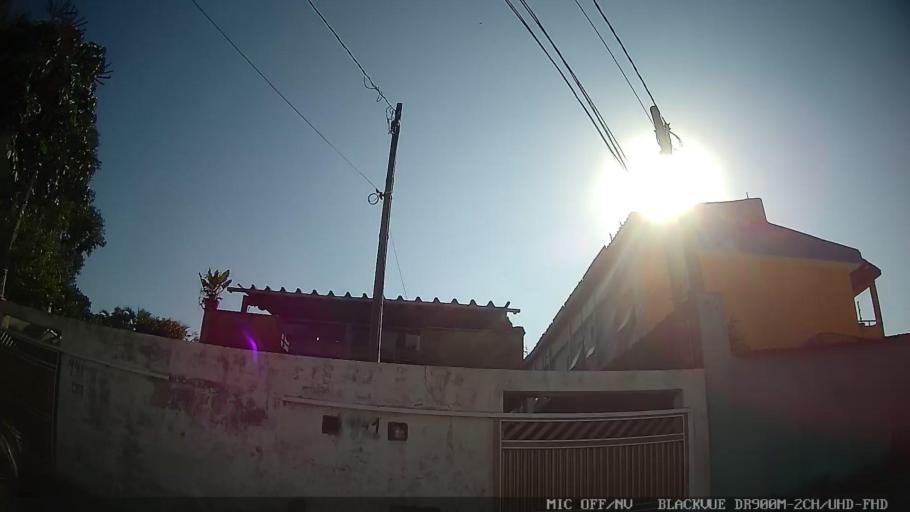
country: BR
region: Sao Paulo
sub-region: Guaruja
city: Guaruja
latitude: -24.0139
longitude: -46.2802
